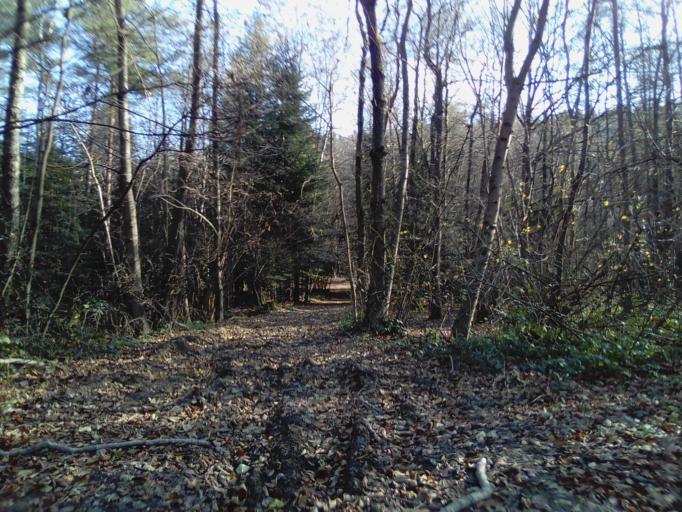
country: PL
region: Subcarpathian Voivodeship
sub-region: Powiat strzyzowski
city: Jawornik
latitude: 49.7908
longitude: 21.8871
